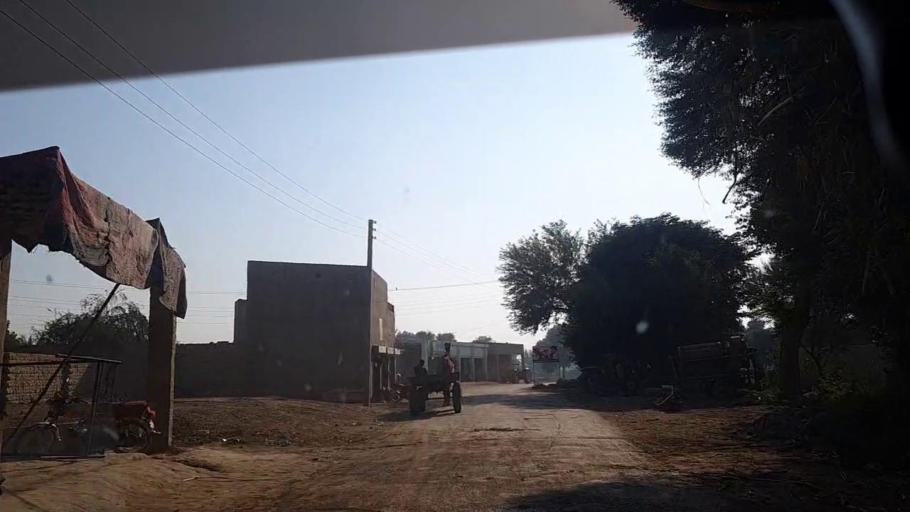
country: PK
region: Sindh
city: Sobhadero
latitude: 27.2518
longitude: 68.2977
